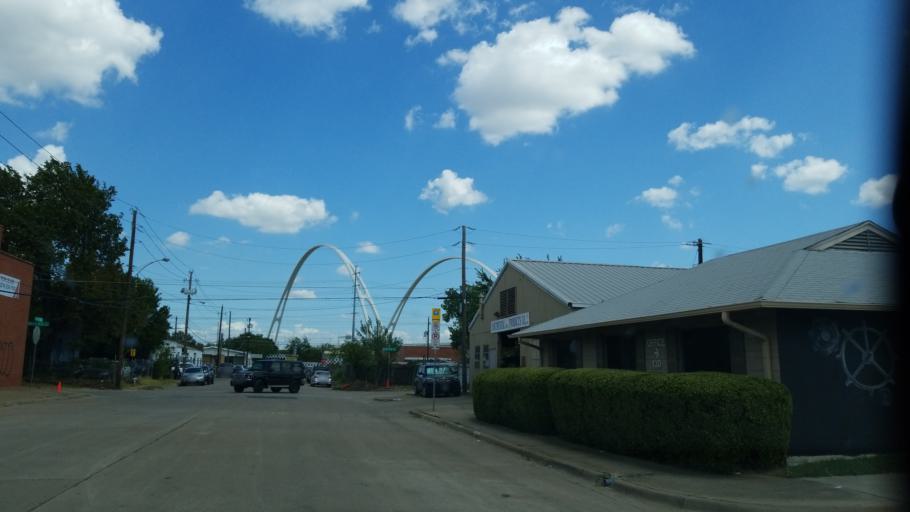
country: US
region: Texas
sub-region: Dallas County
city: Dallas
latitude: 32.7709
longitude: -96.8246
